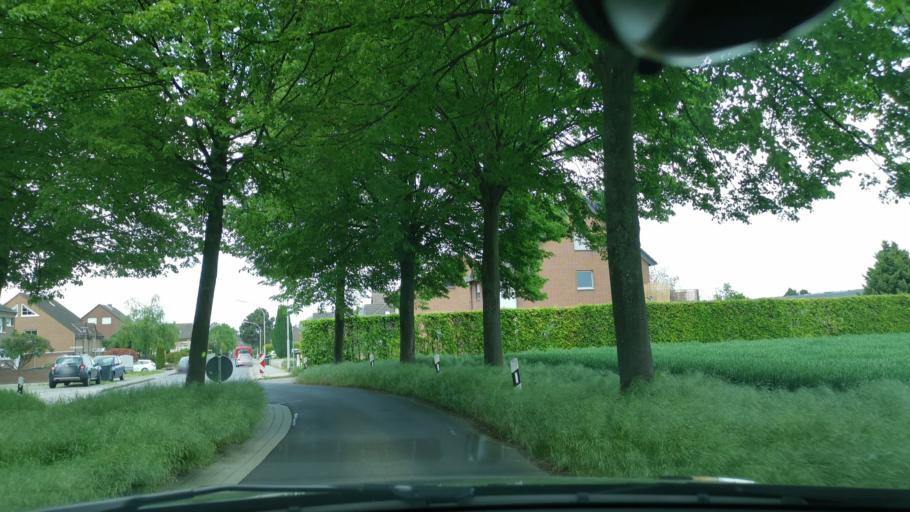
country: DE
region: North Rhine-Westphalia
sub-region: Regierungsbezirk Dusseldorf
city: Rommerskirchen
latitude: 51.0740
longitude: 6.6440
